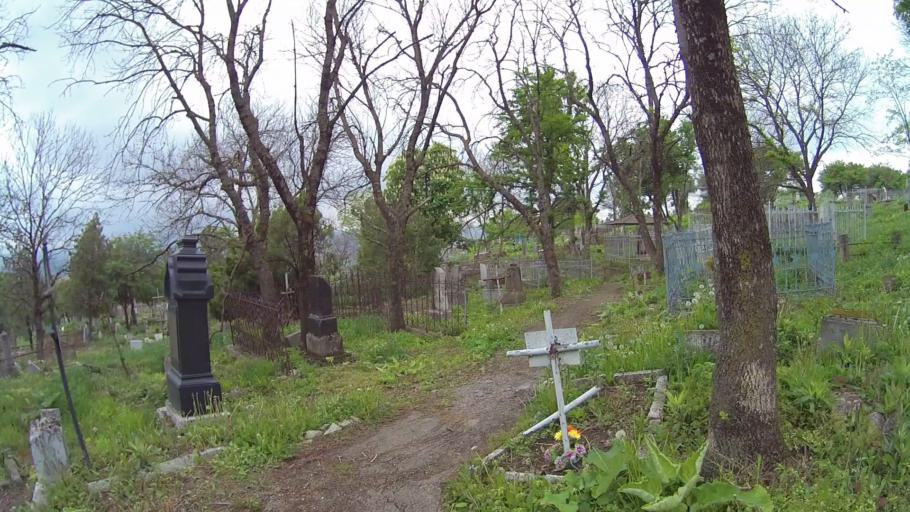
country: RU
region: Stavropol'skiy
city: Pyatigorsk
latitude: 44.0470
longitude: 43.0744
